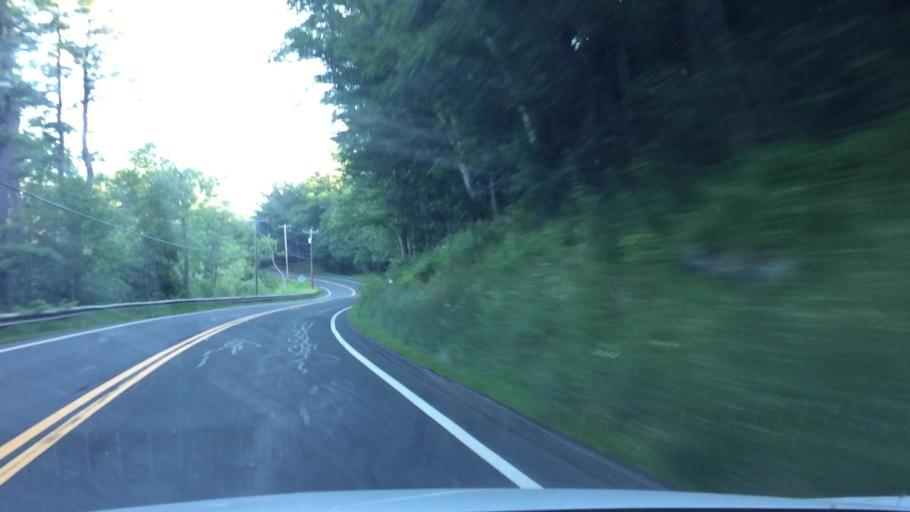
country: US
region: Massachusetts
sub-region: Berkshire County
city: Otis
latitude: 42.2200
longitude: -73.1028
